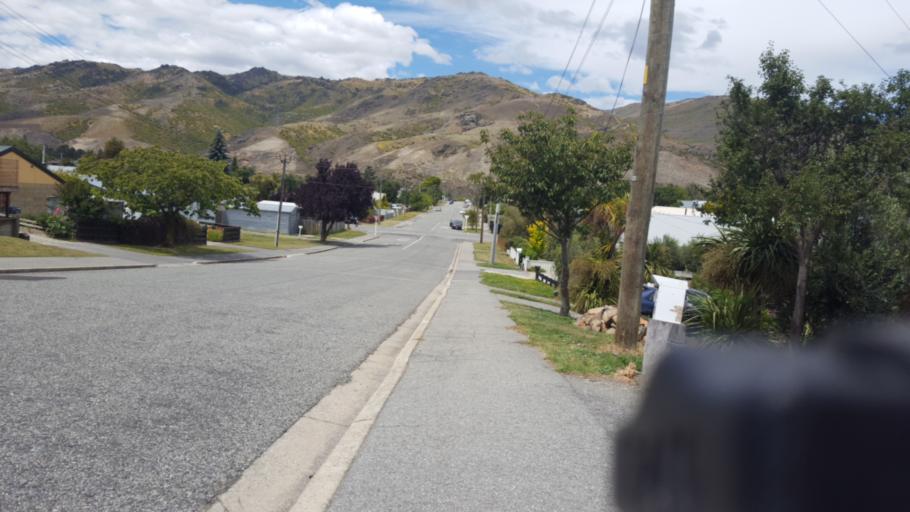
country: NZ
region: Otago
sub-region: Queenstown-Lakes District
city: Wanaka
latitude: -45.0447
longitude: 169.2056
